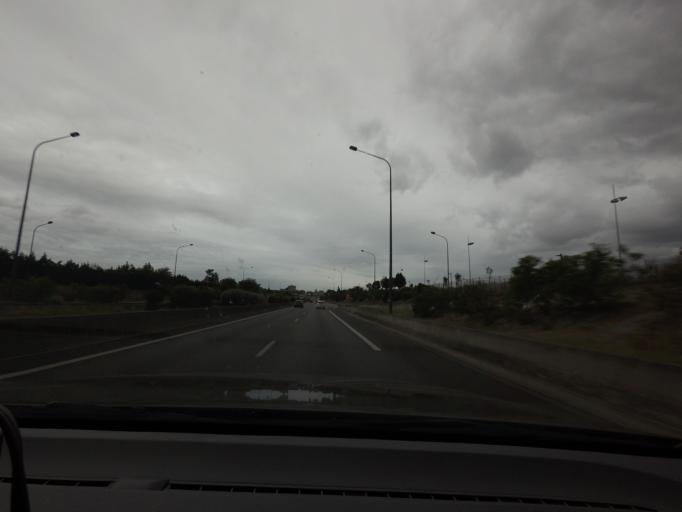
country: FR
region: Midi-Pyrenees
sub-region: Departement de la Haute-Garonne
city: Colomiers
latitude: 43.5961
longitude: 1.3629
